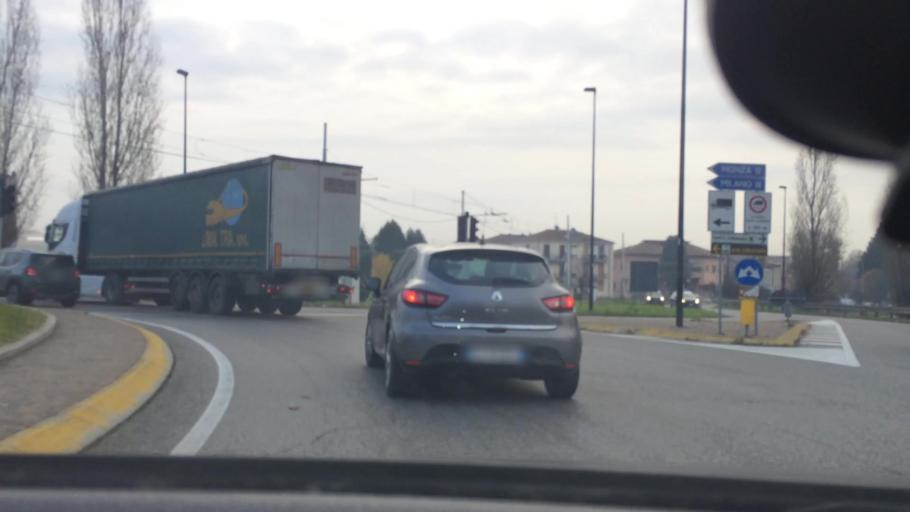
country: IT
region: Lombardy
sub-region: Provincia di Monza e Brianza
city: Limbiate
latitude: 45.6070
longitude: 9.1218
